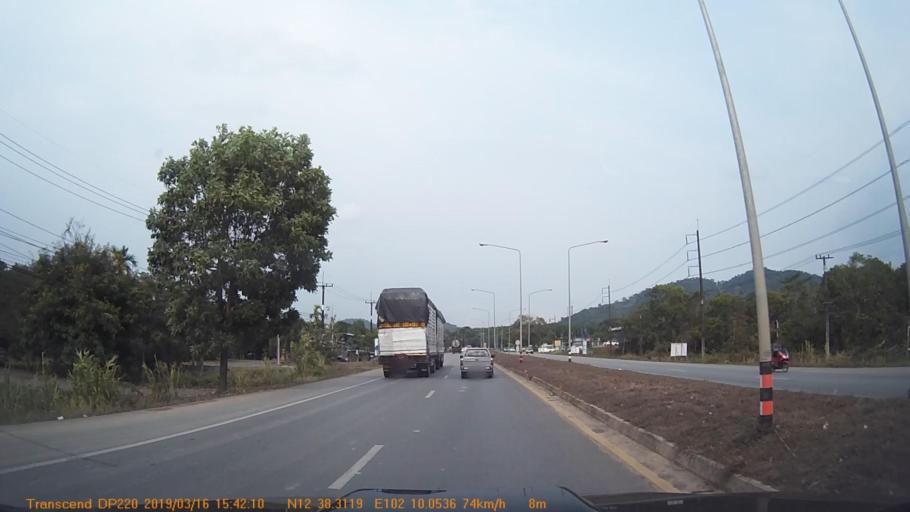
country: TH
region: Chanthaburi
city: Makham
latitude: 12.6386
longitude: 102.1678
